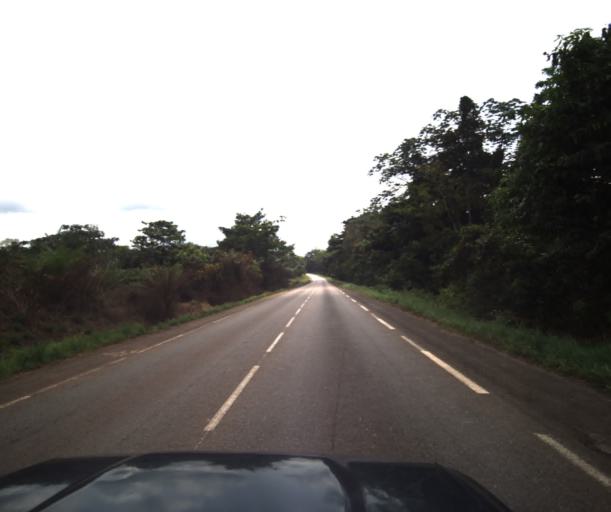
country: CM
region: Centre
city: Eseka
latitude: 3.8716
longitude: 10.6193
